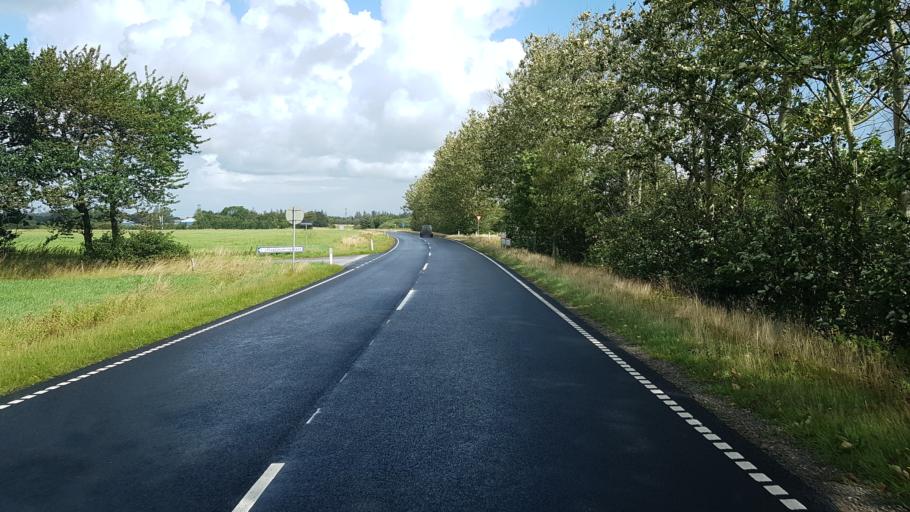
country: DK
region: South Denmark
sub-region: Vejen Kommune
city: Vejen
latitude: 55.4970
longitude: 9.1323
